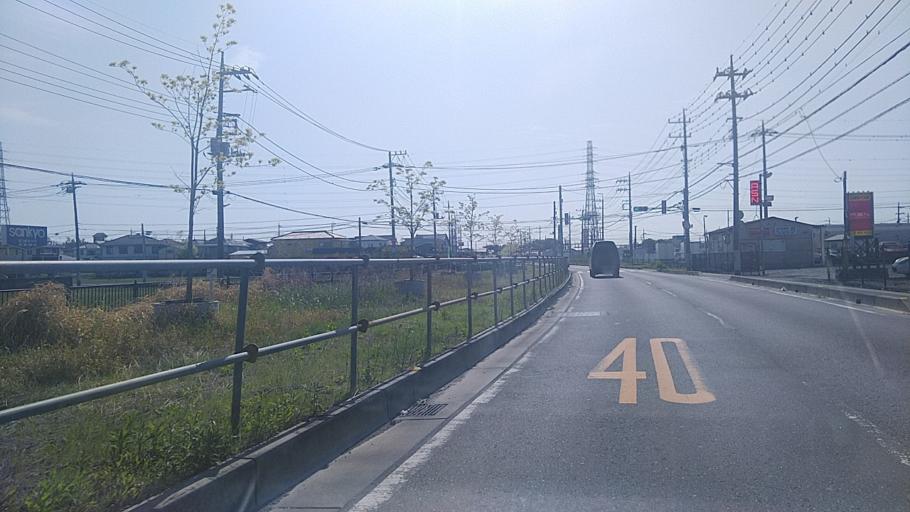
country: JP
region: Saitama
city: Koshigaya
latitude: 35.8696
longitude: 139.7709
